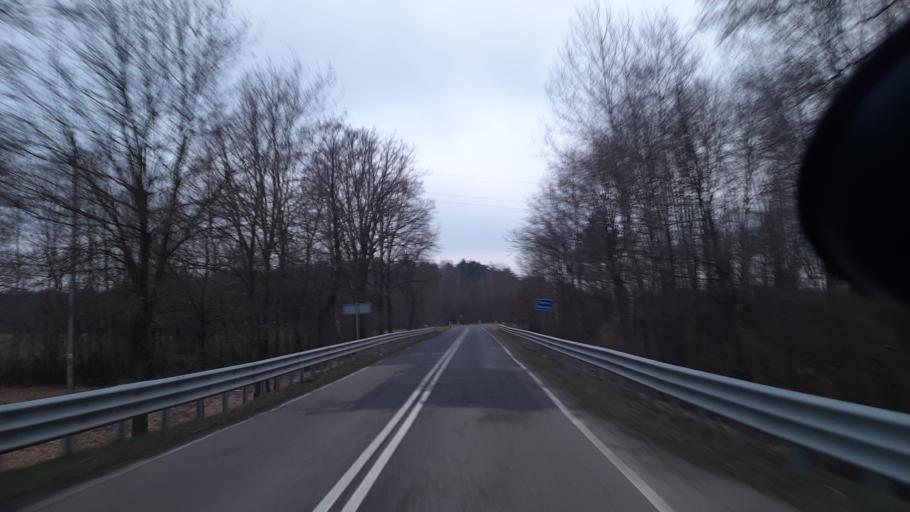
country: PL
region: Lublin Voivodeship
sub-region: Powiat parczewski
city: Debowa Kloda
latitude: 51.6392
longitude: 23.0224
